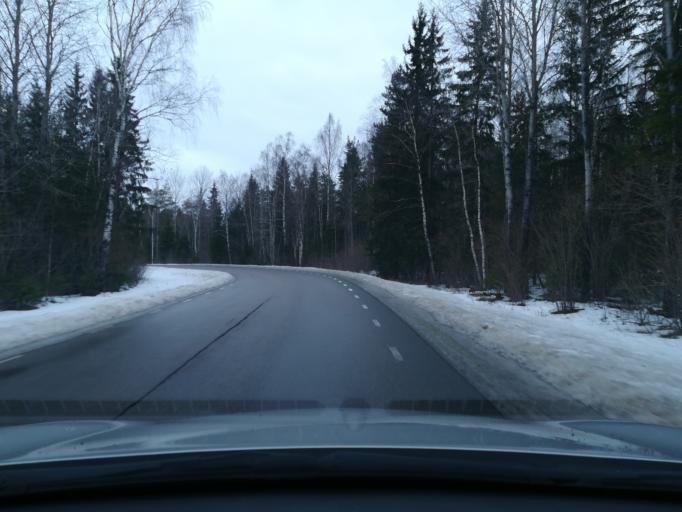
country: EE
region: Harju
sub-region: Nissi vald
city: Riisipere
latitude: 59.1379
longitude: 24.2988
